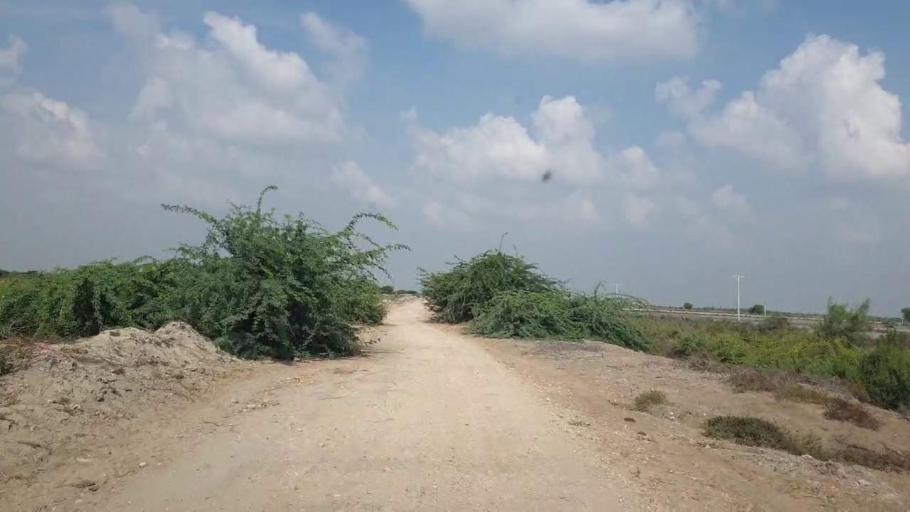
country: PK
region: Sindh
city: Badin
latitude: 24.5032
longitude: 68.6557
